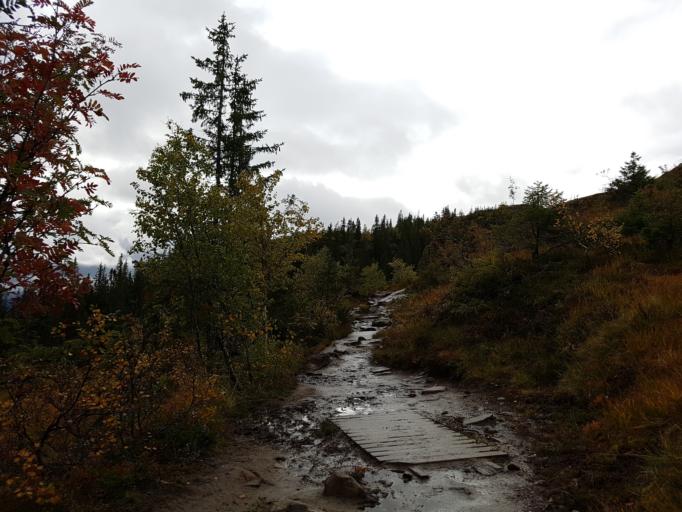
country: NO
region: Sor-Trondelag
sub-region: Melhus
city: Melhus
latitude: 63.4079
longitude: 10.2056
